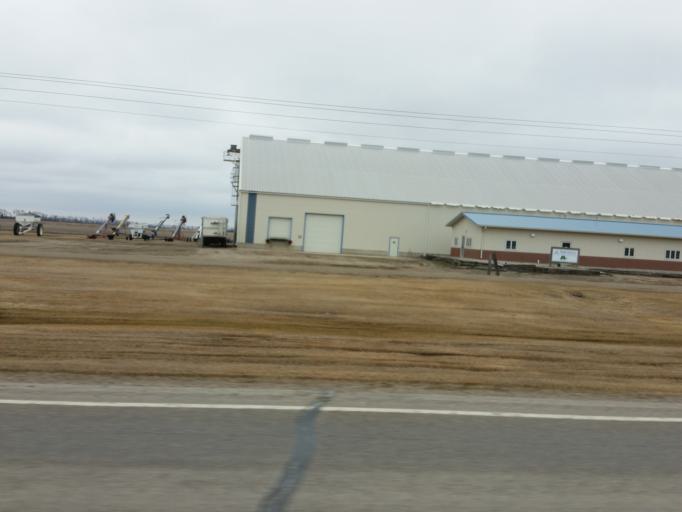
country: US
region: North Dakota
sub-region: Traill County
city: Hillsboro
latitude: 47.1841
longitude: -97.2175
